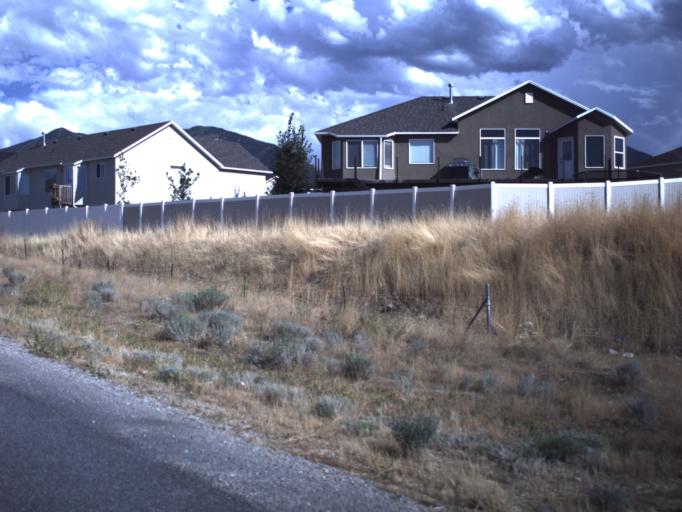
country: US
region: Utah
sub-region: Tooele County
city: Tooele
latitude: 40.5509
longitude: -112.3084
